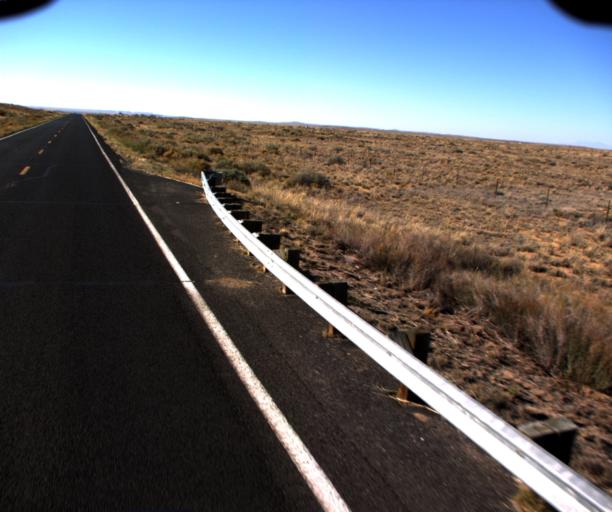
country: US
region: Arizona
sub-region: Navajo County
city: First Mesa
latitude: 35.7728
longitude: -110.5053
